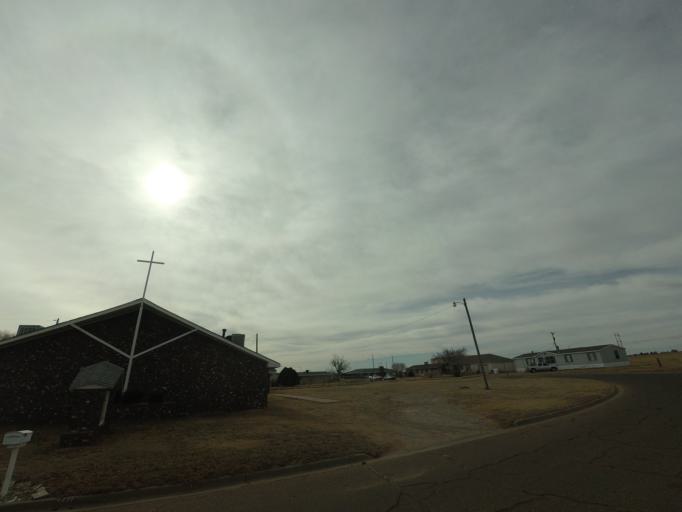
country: US
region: New Mexico
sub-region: Curry County
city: Clovis
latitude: 34.4099
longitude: -103.2462
